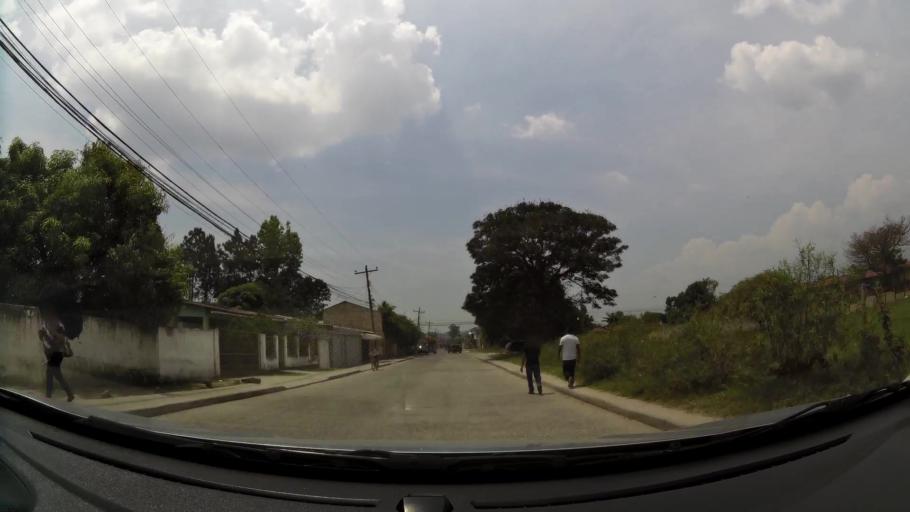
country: HN
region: Comayagua
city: Siguatepeque
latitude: 14.6022
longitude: -87.8379
